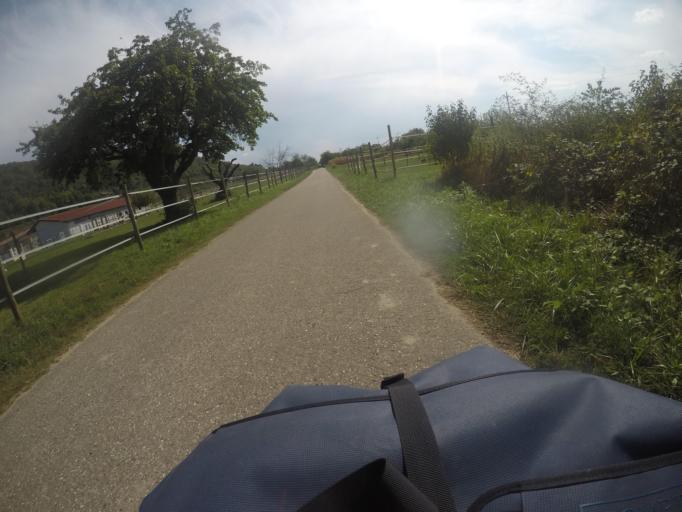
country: FR
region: Alsace
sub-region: Departement du Haut-Rhin
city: Kembs
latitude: 47.6957
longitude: 7.5238
